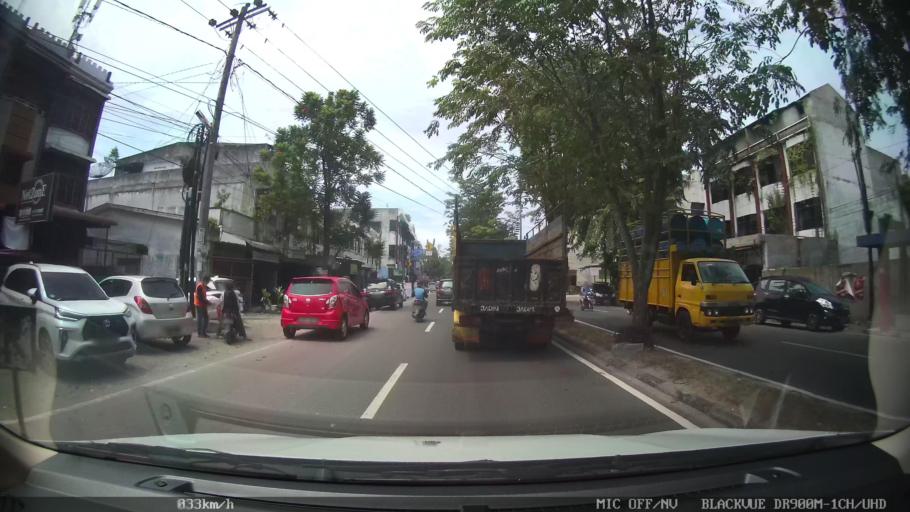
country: ID
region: North Sumatra
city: Sunggal
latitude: 3.5764
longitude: 98.6115
